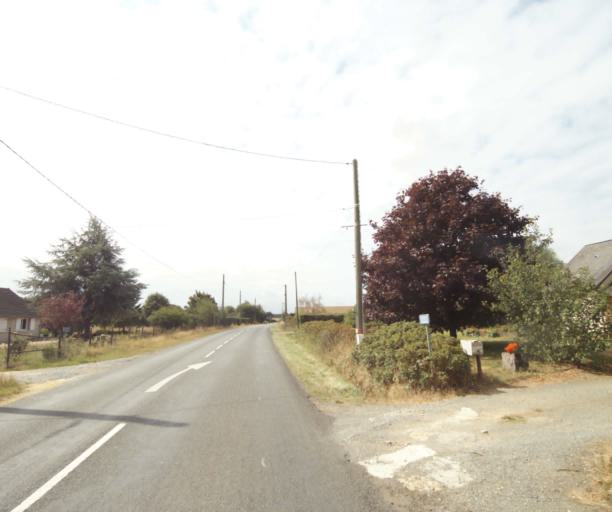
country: FR
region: Pays de la Loire
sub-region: Departement de la Sarthe
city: Sable-sur-Sarthe
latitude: 47.8106
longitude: -0.3180
